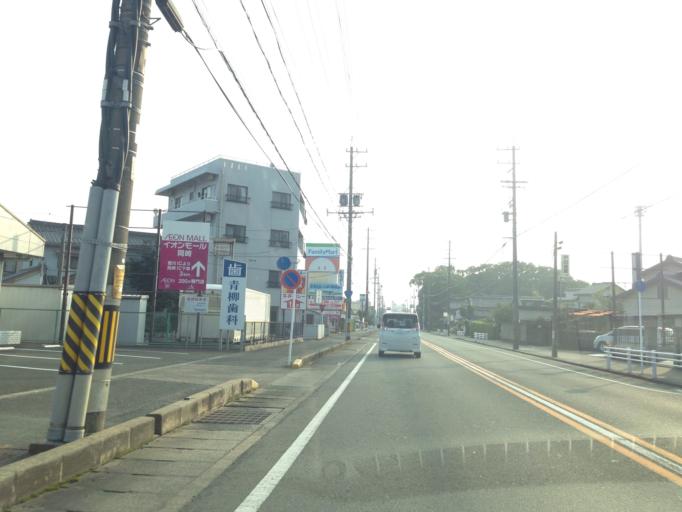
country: JP
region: Aichi
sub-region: Tokai-shi
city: Toyokawa
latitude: 34.8434
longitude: 137.4152
